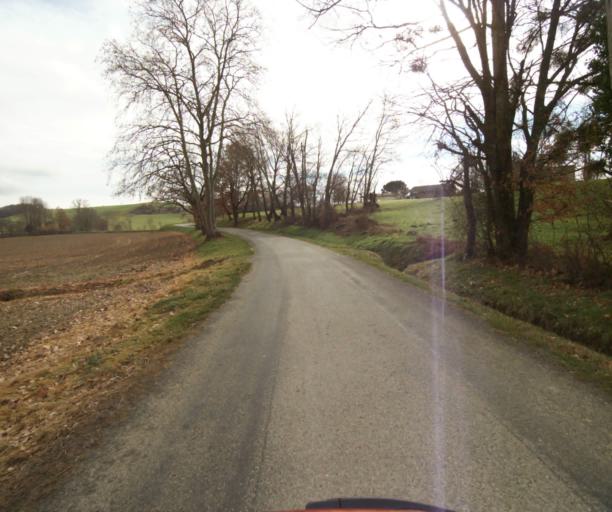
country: FR
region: Midi-Pyrenees
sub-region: Departement de l'Ariege
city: Pamiers
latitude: 43.1028
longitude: 1.5520
